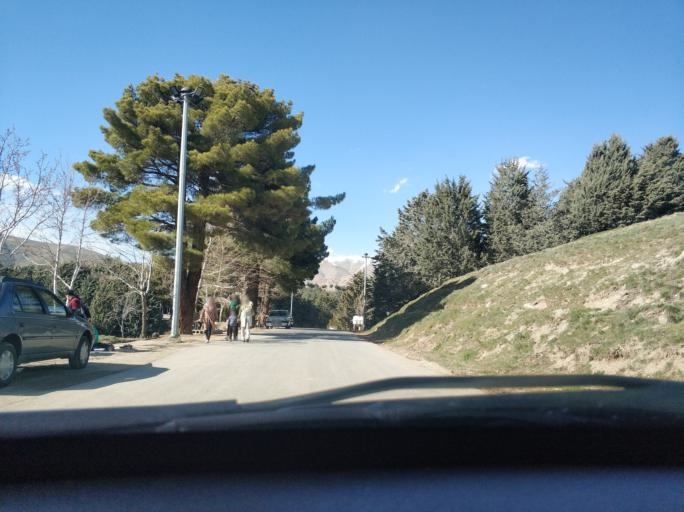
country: IR
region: Tehran
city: Tajrish
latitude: 35.8011
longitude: 51.5674
